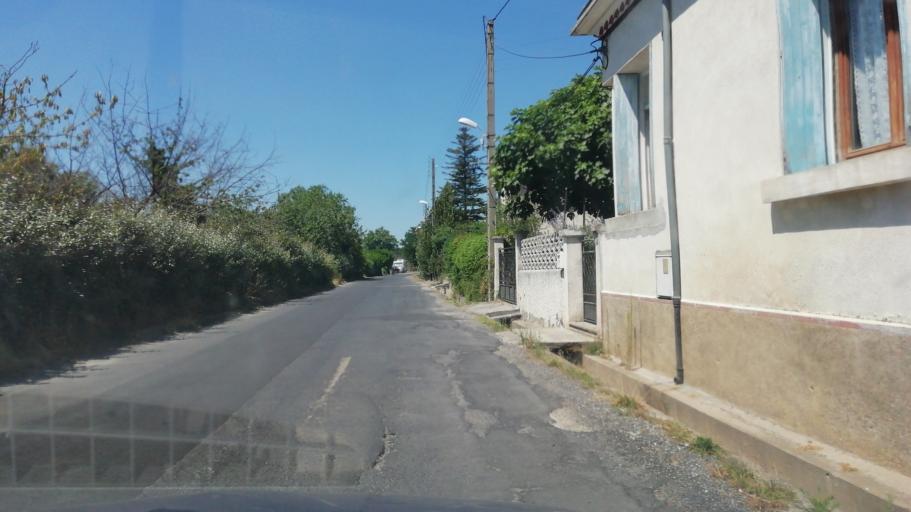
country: FR
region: Languedoc-Roussillon
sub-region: Departement de l'Herault
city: Capestang
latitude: 43.3308
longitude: 3.0482
